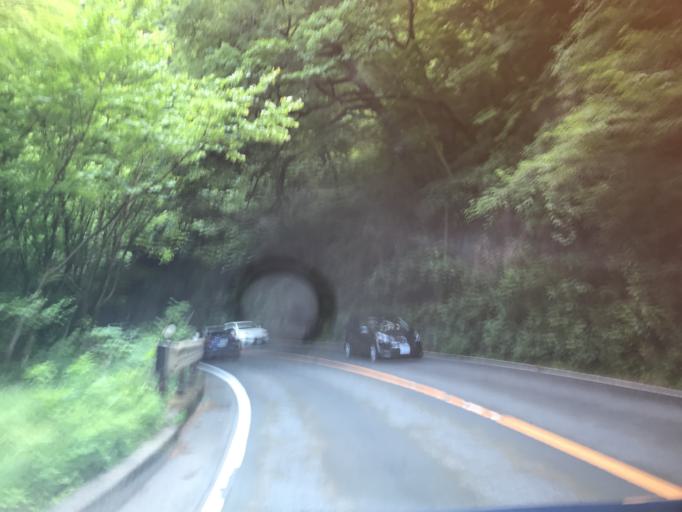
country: JP
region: Kanagawa
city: Hakone
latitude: 35.2334
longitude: 139.0867
